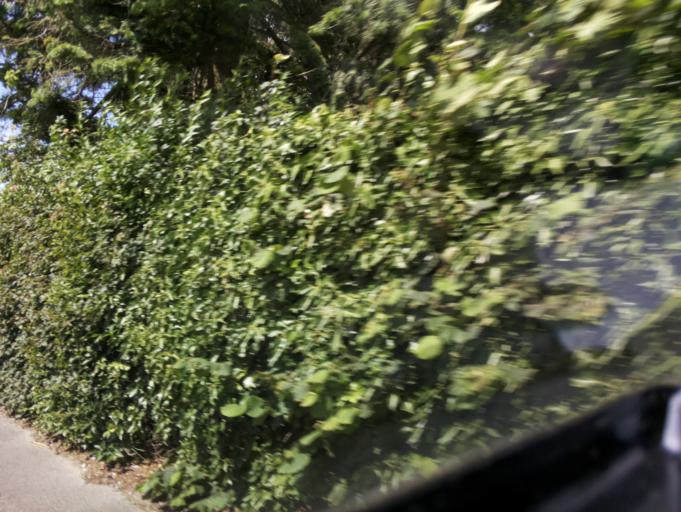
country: GB
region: England
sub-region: Nottinghamshire
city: Arnold
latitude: 53.0069
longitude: -1.0837
